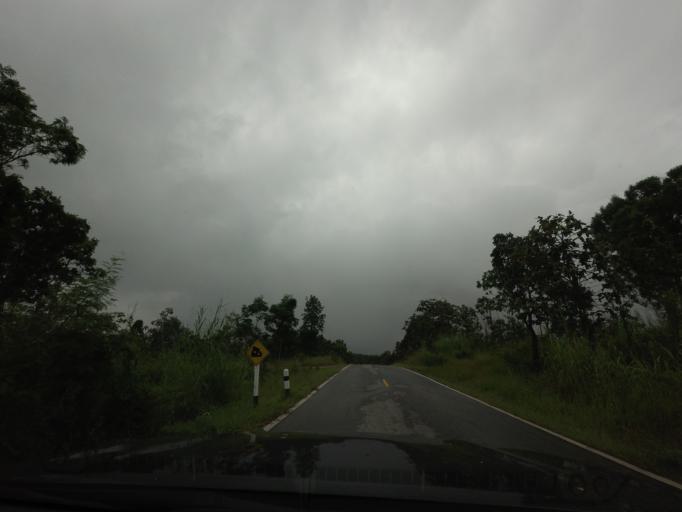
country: TH
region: Nong Khai
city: Sangkhom
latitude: 18.0360
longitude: 102.3349
